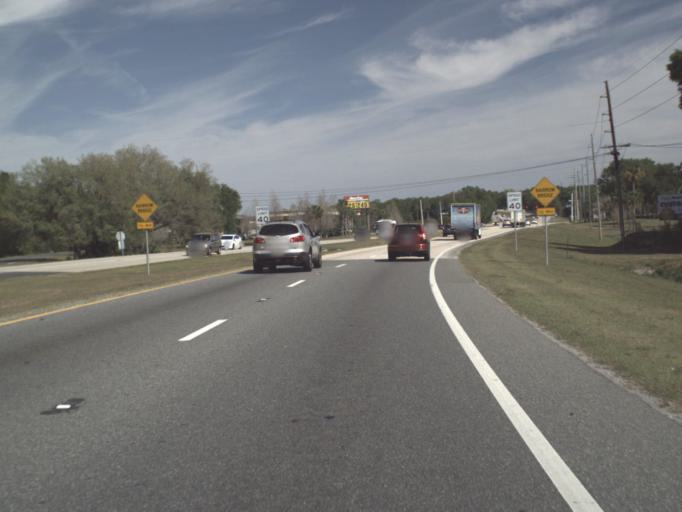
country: US
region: Florida
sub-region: Lake County
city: Lady Lake
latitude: 28.9206
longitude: -81.9241
